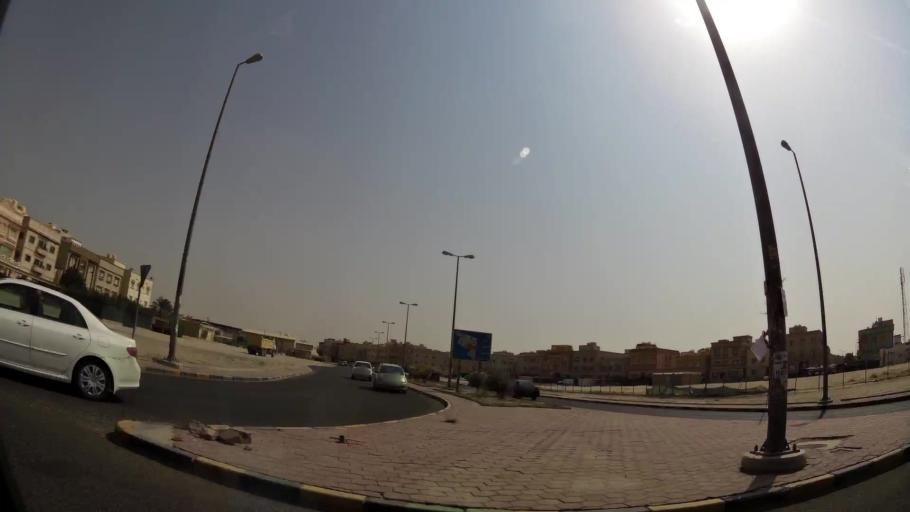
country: KW
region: Muhafazat al Jahra'
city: Al Jahra'
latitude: 29.3083
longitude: 47.7052
